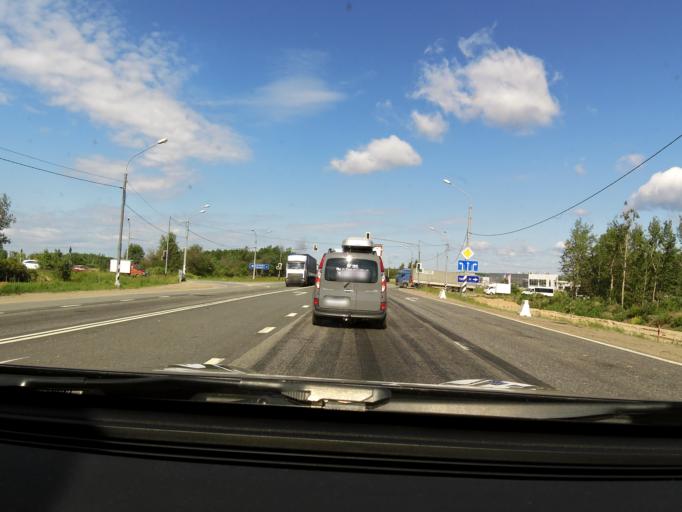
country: RU
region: Tverskaya
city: Tver
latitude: 56.7881
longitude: 35.9162
